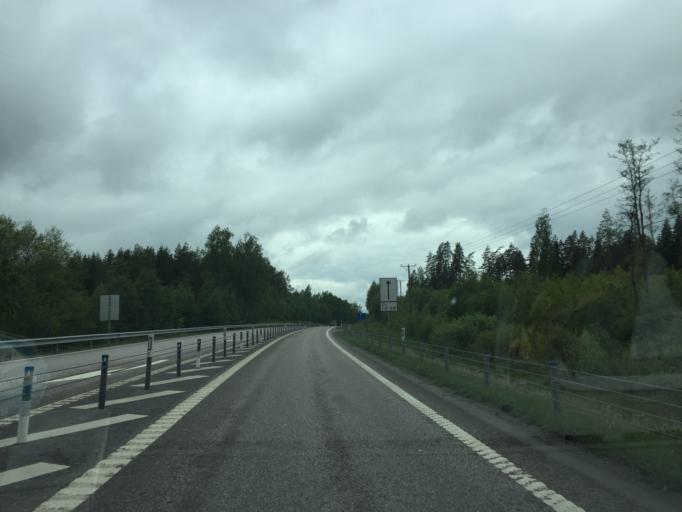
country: SE
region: Soedermanland
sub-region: Katrineholms Kommun
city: Katrineholm
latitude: 59.0219
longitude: 16.3599
